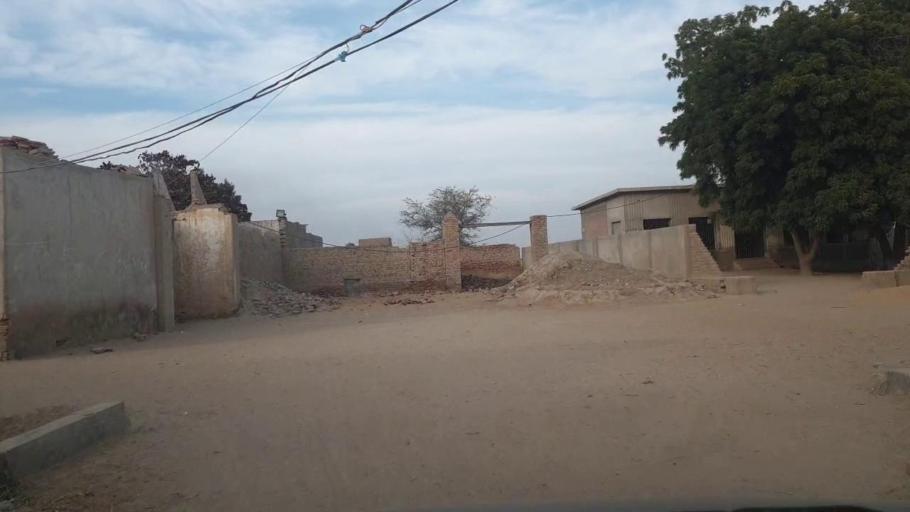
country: PK
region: Sindh
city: Shahpur Chakar
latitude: 26.1389
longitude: 68.6082
